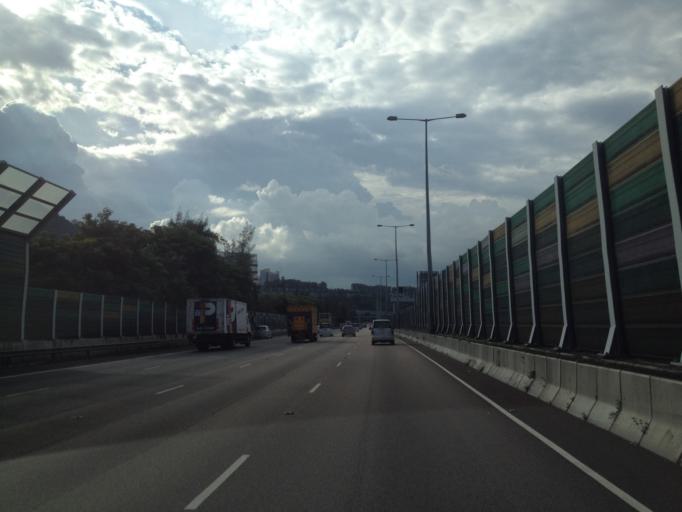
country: HK
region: Tai Po
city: Tai Po
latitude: 22.4261
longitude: 114.2081
